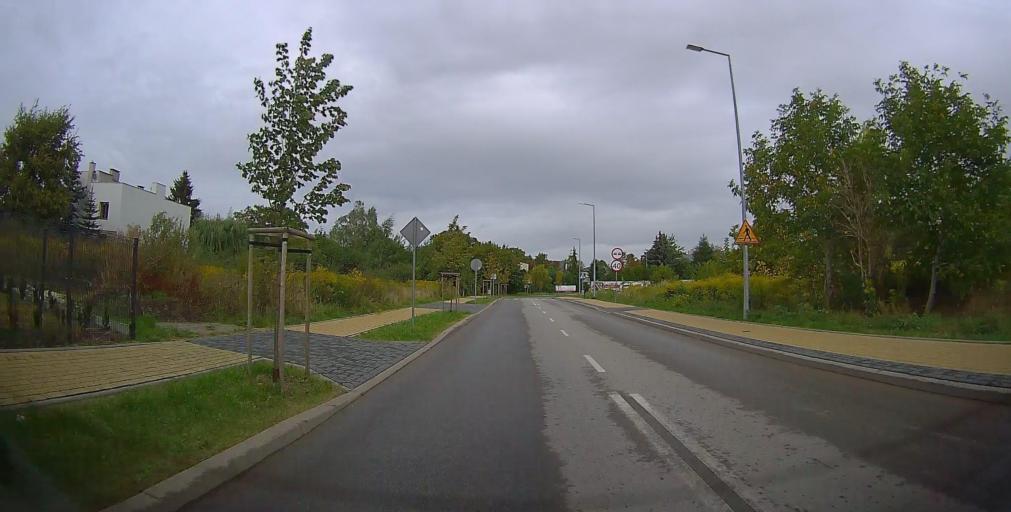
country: PL
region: Masovian Voivodeship
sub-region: Powiat grojecki
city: Grojec
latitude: 51.8632
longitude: 20.8744
